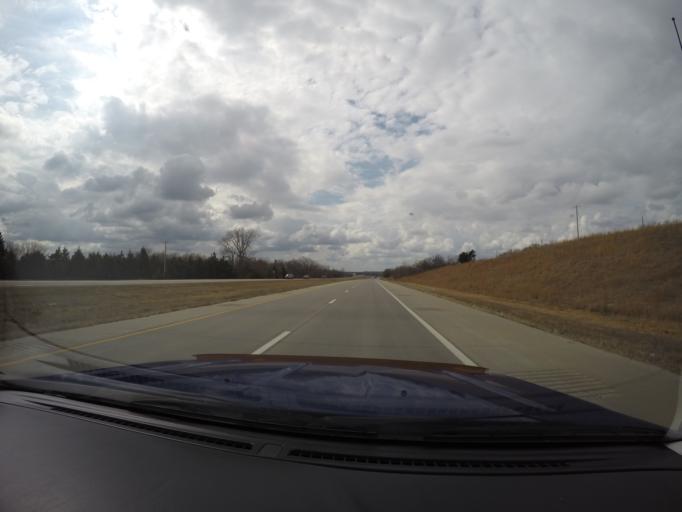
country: US
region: Kansas
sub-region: Riley County
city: Manhattan
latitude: 39.1979
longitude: -96.4723
